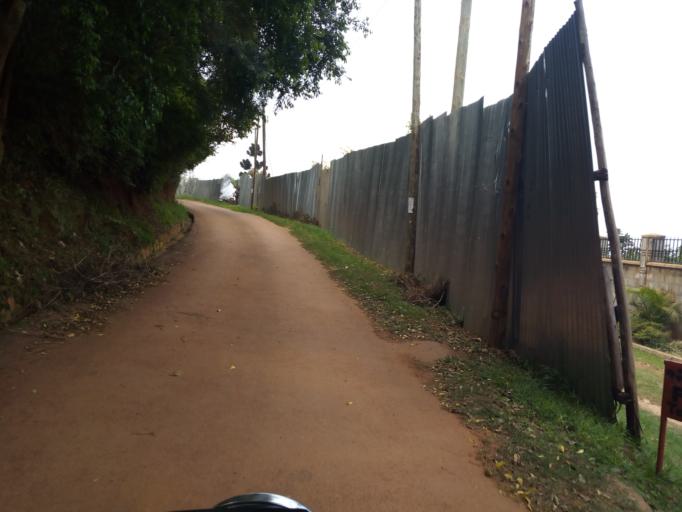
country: UG
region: Central Region
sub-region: Wakiso District
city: Kireka
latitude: 0.3256
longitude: 32.6325
